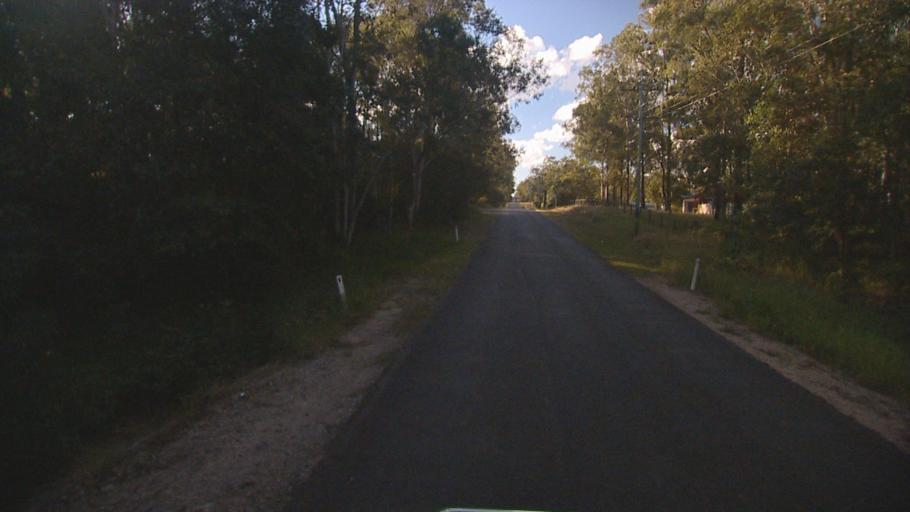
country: AU
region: Queensland
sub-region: Ipswich
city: Springfield Lakes
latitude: -27.7101
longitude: 152.9467
